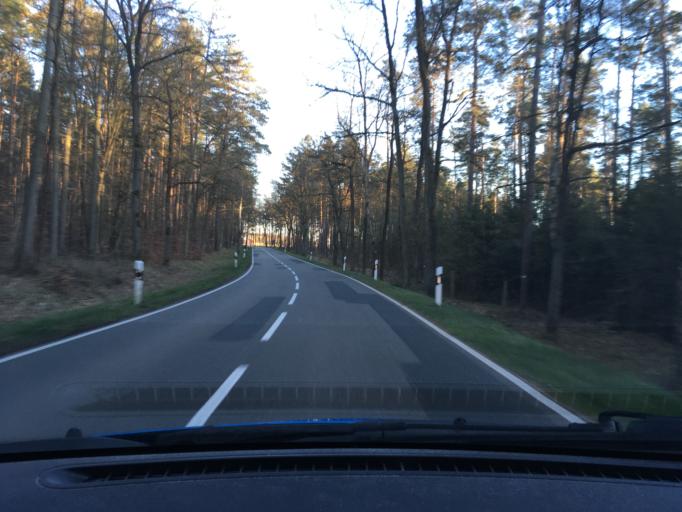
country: DE
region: Lower Saxony
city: Dahlem
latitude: 53.2394
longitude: 10.7510
